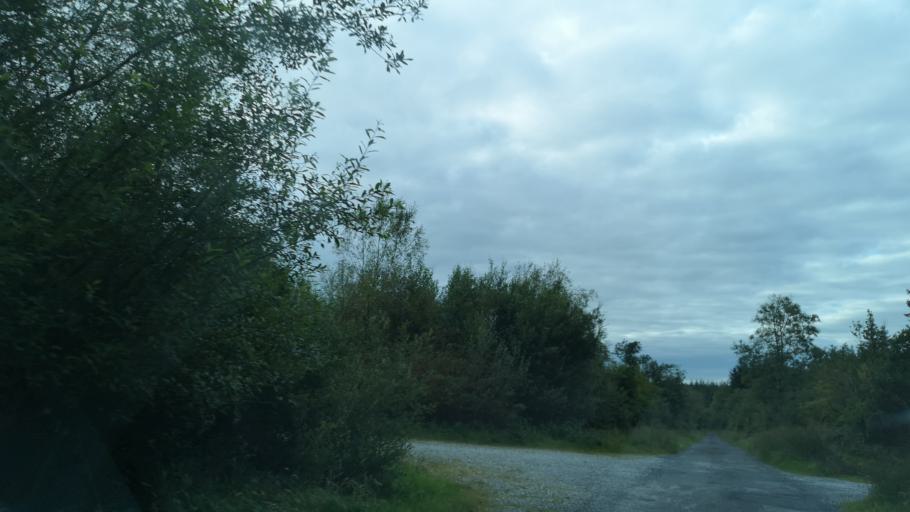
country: IE
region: Connaught
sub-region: County Galway
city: Loughrea
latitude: 53.1356
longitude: -8.5210
